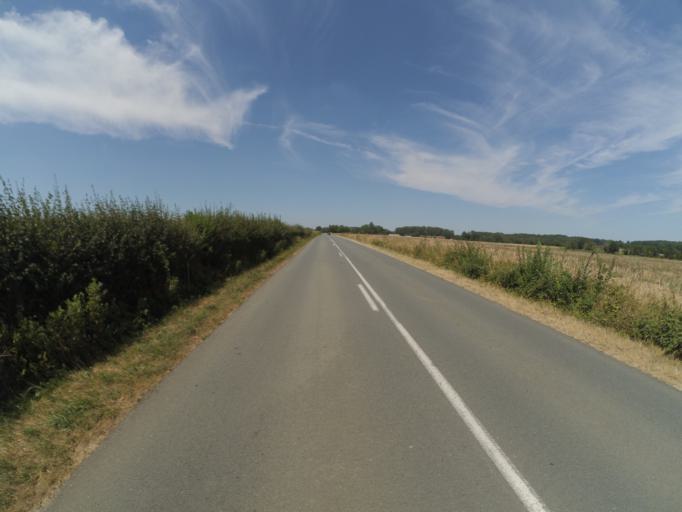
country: FR
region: Poitou-Charentes
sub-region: Departement de la Vienne
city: Usson-du-Poitou
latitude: 46.3153
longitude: 0.4919
